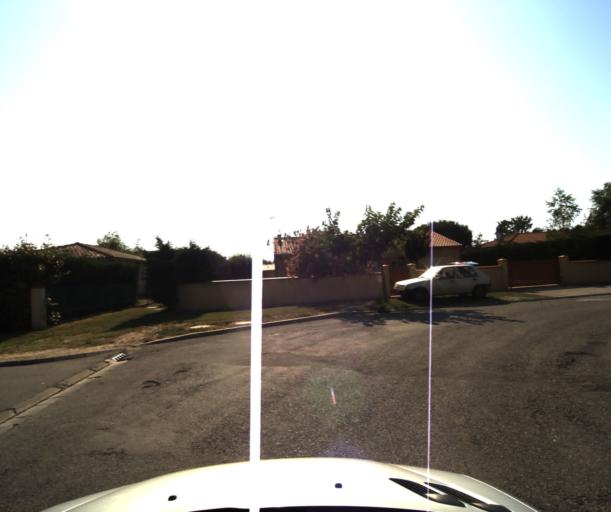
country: FR
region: Midi-Pyrenees
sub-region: Departement de la Haute-Garonne
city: Lacroix-Falgarde
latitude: 43.4784
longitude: 1.3963
